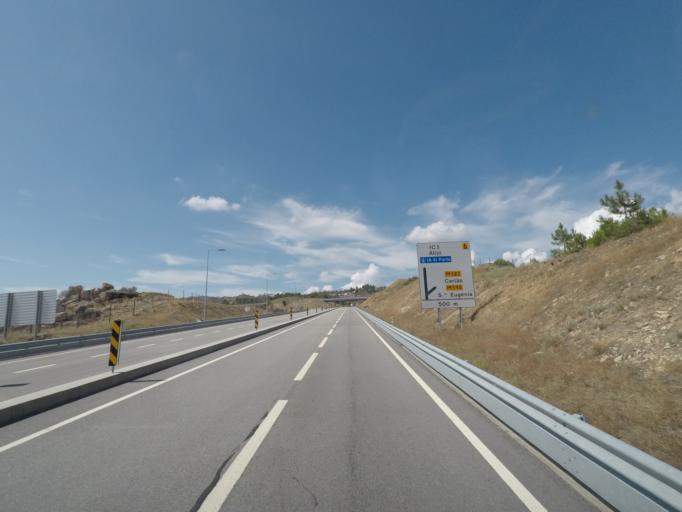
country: PT
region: Vila Real
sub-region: Murca
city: Murca
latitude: 41.3298
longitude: -7.4325
